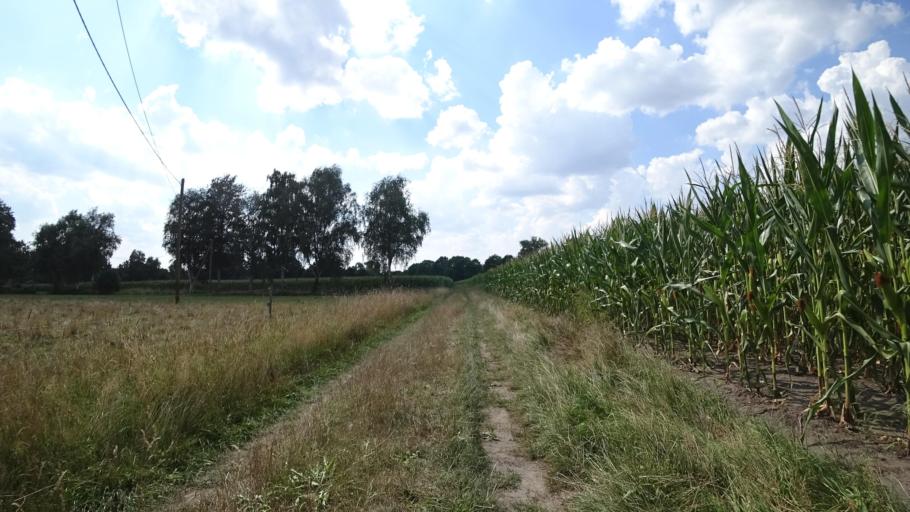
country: DE
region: North Rhine-Westphalia
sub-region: Regierungsbezirk Detmold
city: Guetersloh
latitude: 51.9249
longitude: 8.4172
